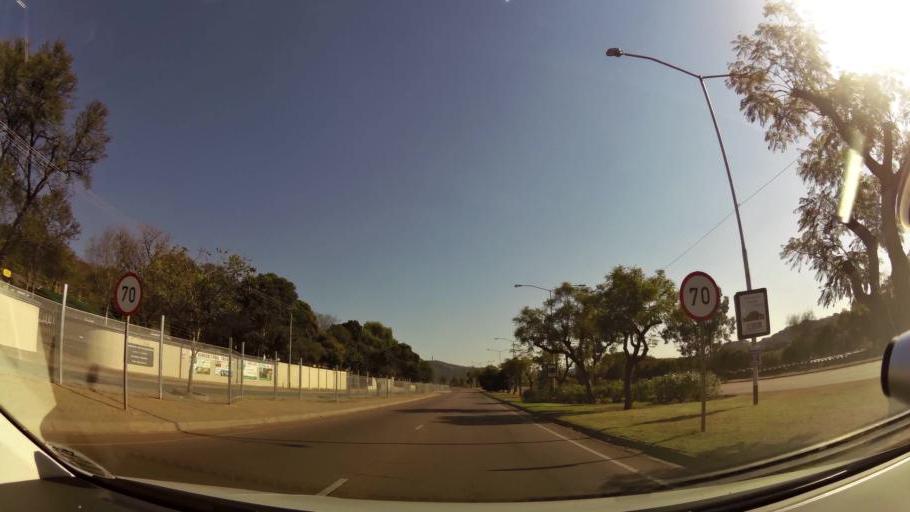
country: ZA
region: Gauteng
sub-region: City of Tshwane Metropolitan Municipality
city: Pretoria
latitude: -25.7715
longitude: 28.2098
